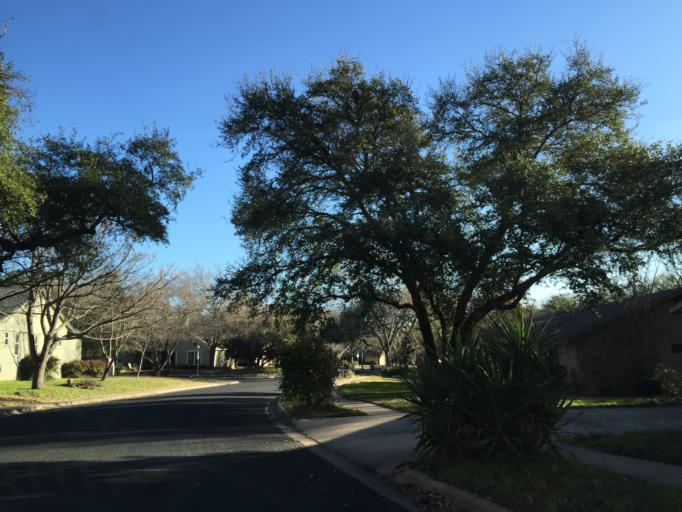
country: US
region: Texas
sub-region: Williamson County
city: Jollyville
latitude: 30.4075
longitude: -97.7413
